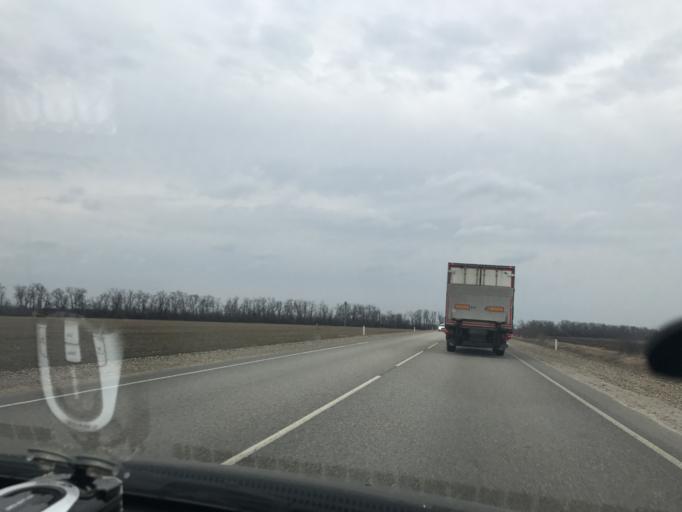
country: RU
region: Krasnodarskiy
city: Alekseyevskaya
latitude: 45.8007
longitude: 40.2130
